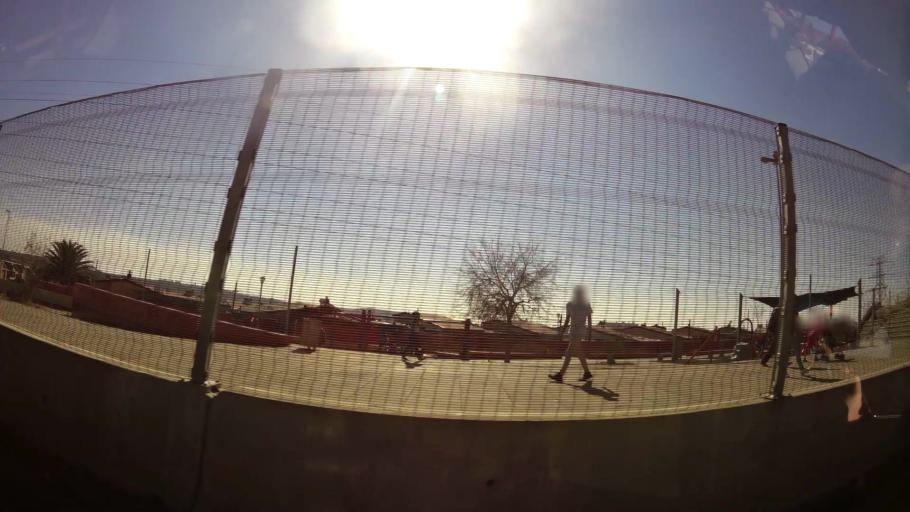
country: ZA
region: Gauteng
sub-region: City of Johannesburg Metropolitan Municipality
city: Johannesburg
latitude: -26.1867
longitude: 27.9763
